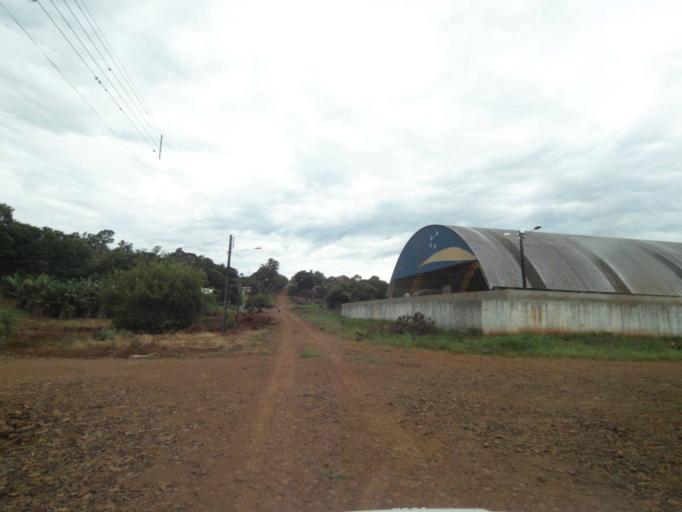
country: BR
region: Parana
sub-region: Guaraniacu
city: Guaraniacu
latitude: -24.9189
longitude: -52.9361
